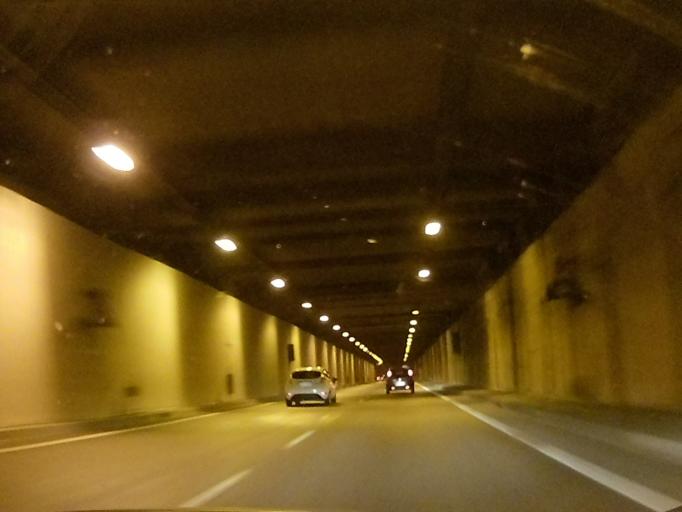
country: IT
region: Lombardy
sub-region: Provincia di Bergamo
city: Ghiaie
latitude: 45.6791
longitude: 9.5749
